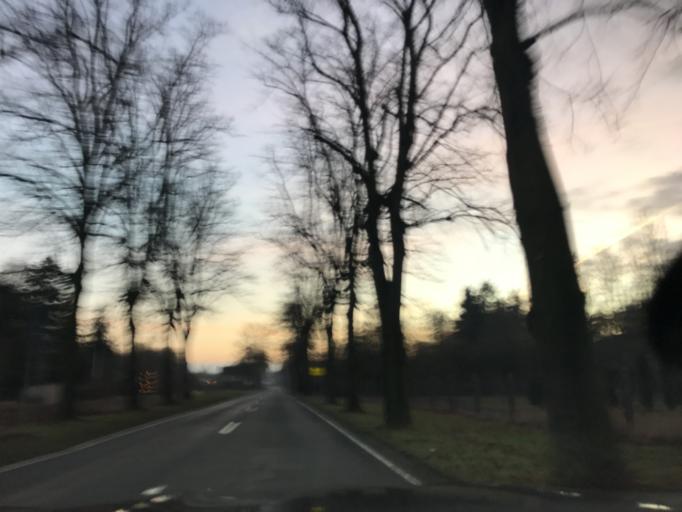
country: DE
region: Brandenburg
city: Ketzin
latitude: 52.4889
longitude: 12.8492
